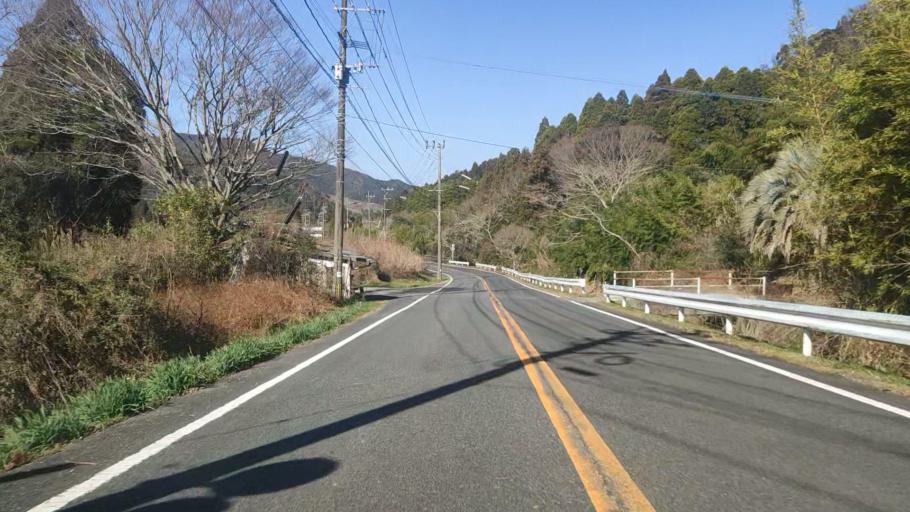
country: JP
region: Oita
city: Saiki
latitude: 32.8986
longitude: 131.9361
